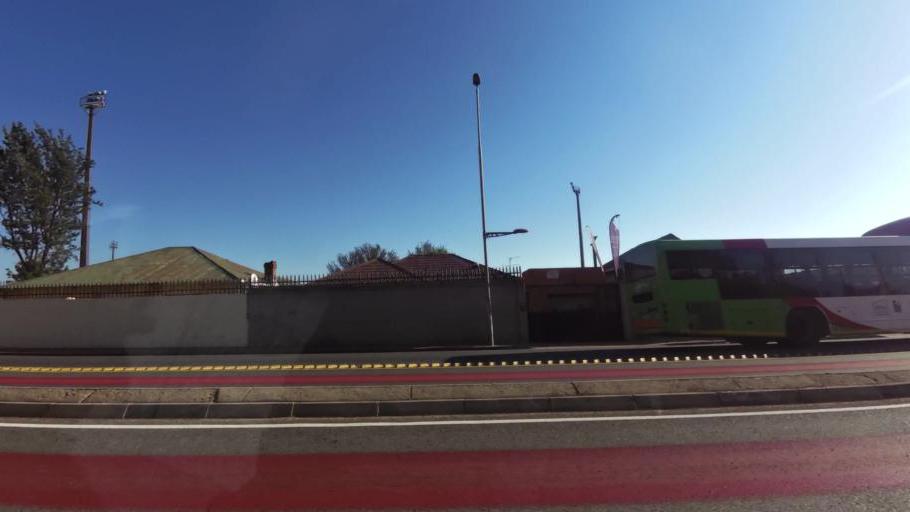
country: ZA
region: Gauteng
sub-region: City of Johannesburg Metropolitan Municipality
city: Johannesburg
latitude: -26.1846
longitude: 27.9869
